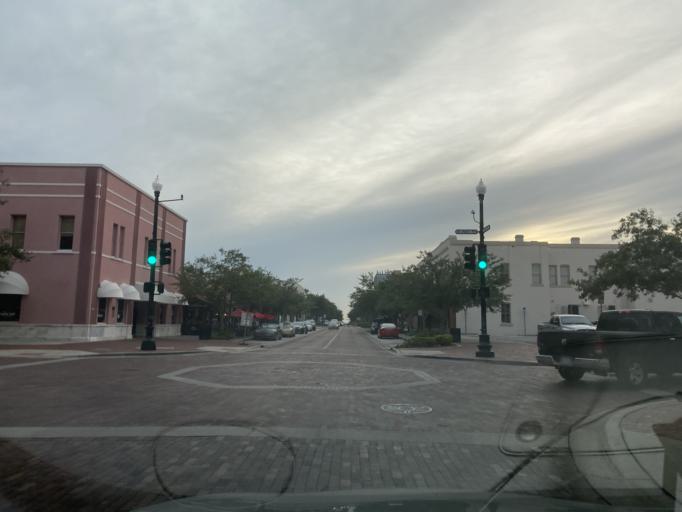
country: US
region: Florida
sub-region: Seminole County
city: Sanford
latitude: 28.8117
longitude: -81.2678
